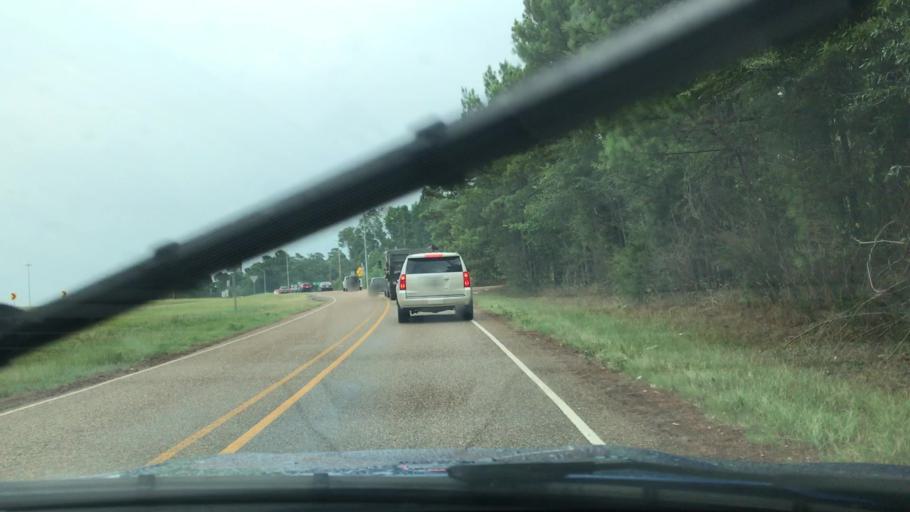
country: US
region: Texas
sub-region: Harrison County
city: Waskom
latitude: 32.4788
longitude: -94.0902
